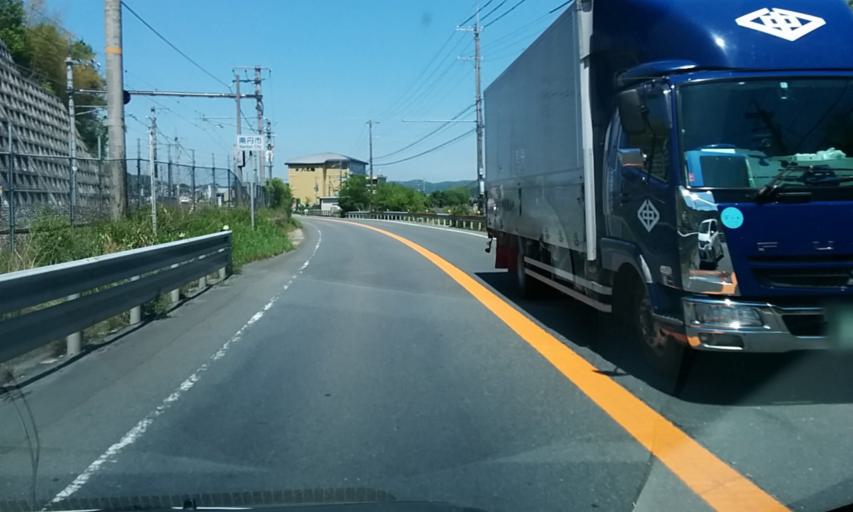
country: JP
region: Kyoto
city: Kameoka
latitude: 35.0658
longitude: 135.5405
